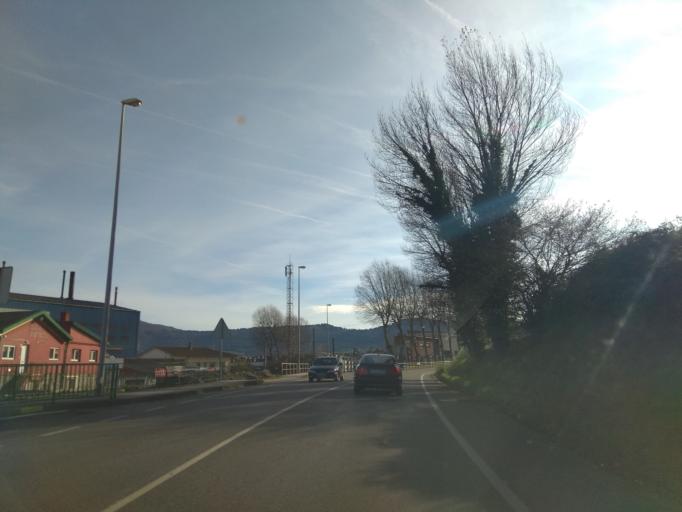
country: ES
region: Cantabria
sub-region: Provincia de Cantabria
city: El Astillero
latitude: 43.4111
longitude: -3.8427
